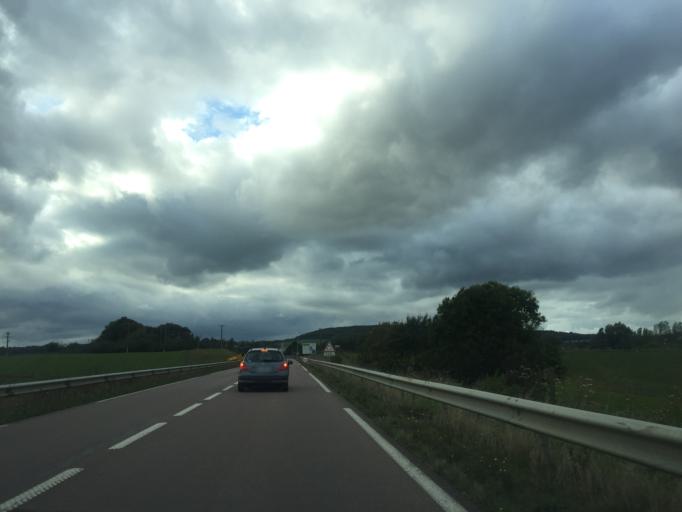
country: FR
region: Lorraine
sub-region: Departement des Vosges
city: Chatenois
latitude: 48.2968
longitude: 5.8556
